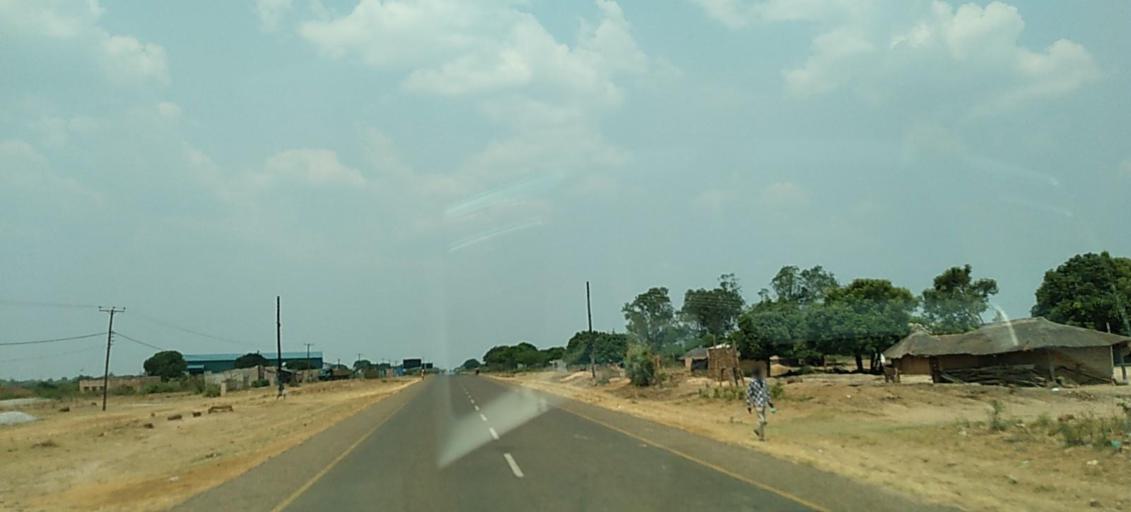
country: ZM
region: North-Western
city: Zambezi
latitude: -13.5507
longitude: 23.1201
